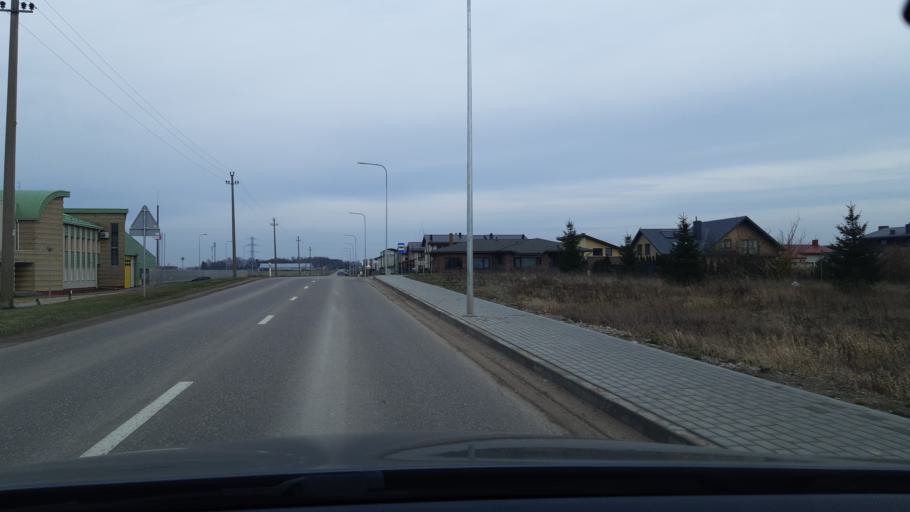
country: LT
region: Kauno apskritis
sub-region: Kaunas
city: Sargenai
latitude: 54.9510
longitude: 23.8472
